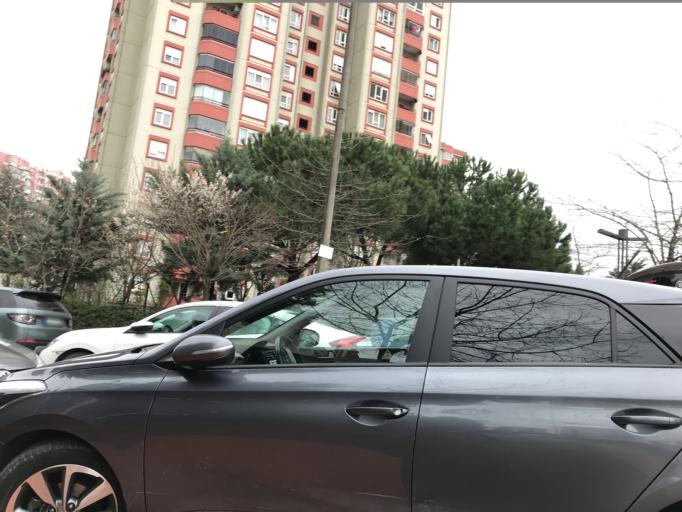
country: TR
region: Istanbul
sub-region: Atasehir
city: Atasehir
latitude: 40.9908
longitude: 29.1225
